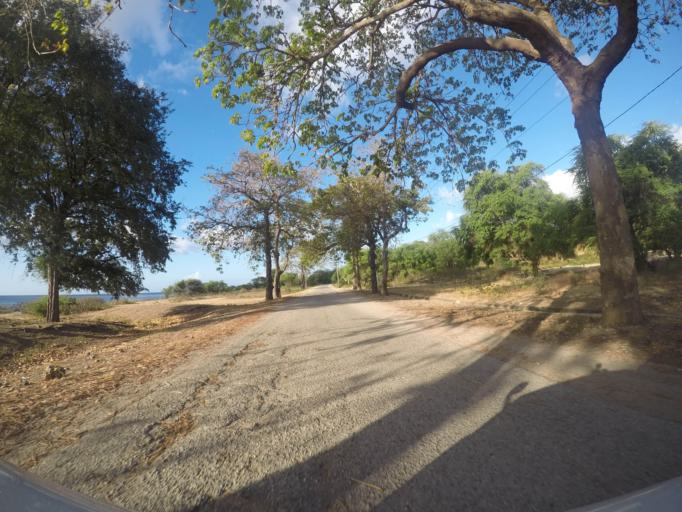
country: TL
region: Lautem
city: Lospalos
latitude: -8.3592
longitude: 126.9076
